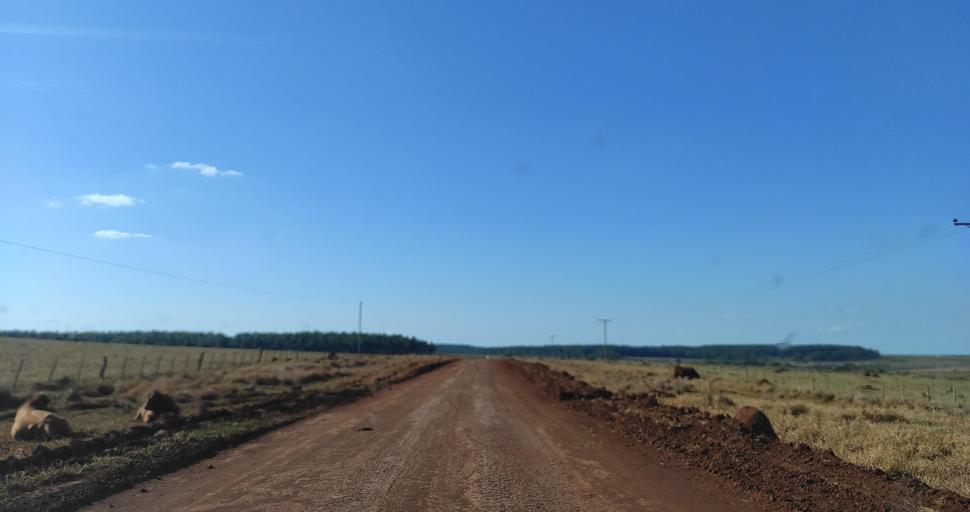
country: PY
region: Itapua
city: San Juan del Parana
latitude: -27.4294
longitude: -56.0834
